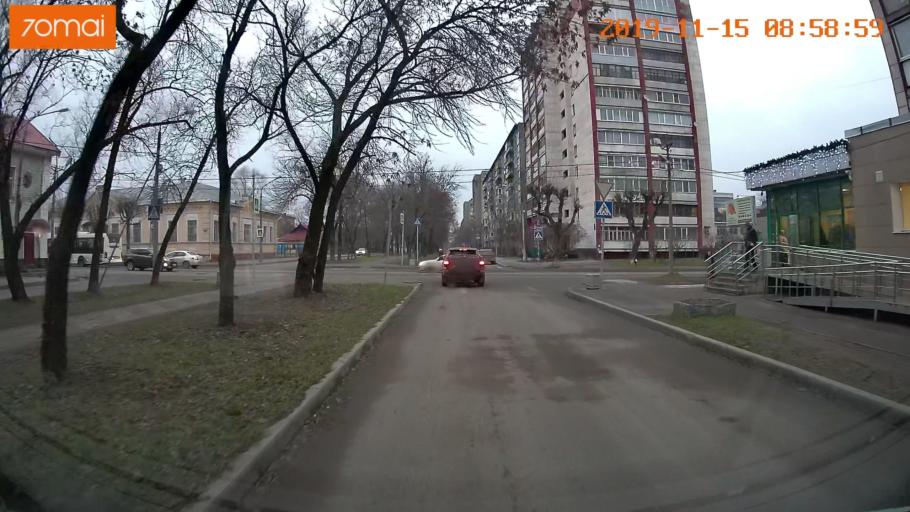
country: RU
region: Vologda
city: Cherepovets
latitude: 59.1278
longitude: 37.9238
